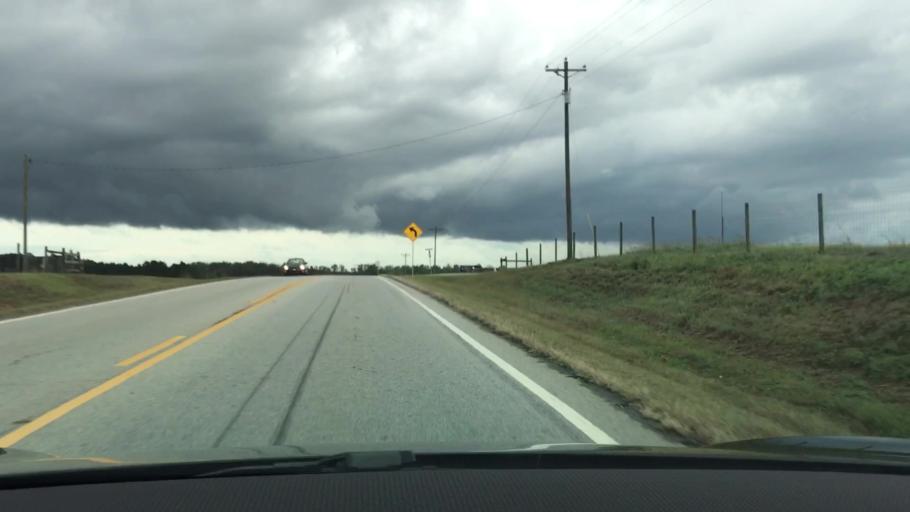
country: US
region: Georgia
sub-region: Oconee County
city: Watkinsville
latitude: 33.7277
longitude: -83.3024
